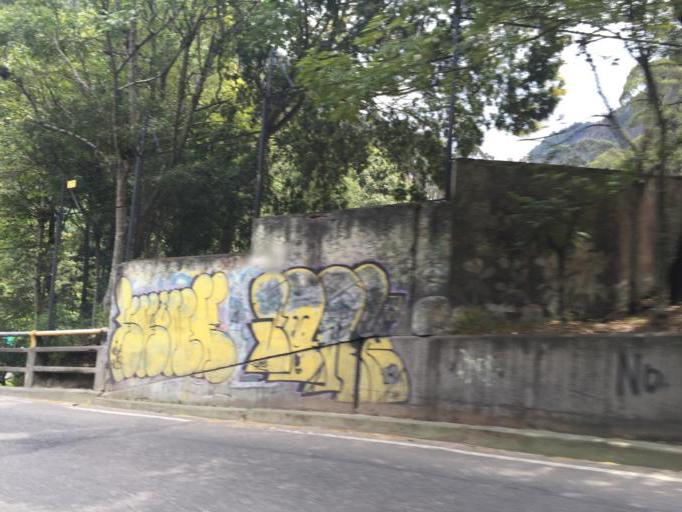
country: CO
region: Bogota D.C.
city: Bogota
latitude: 4.6017
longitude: -74.0602
